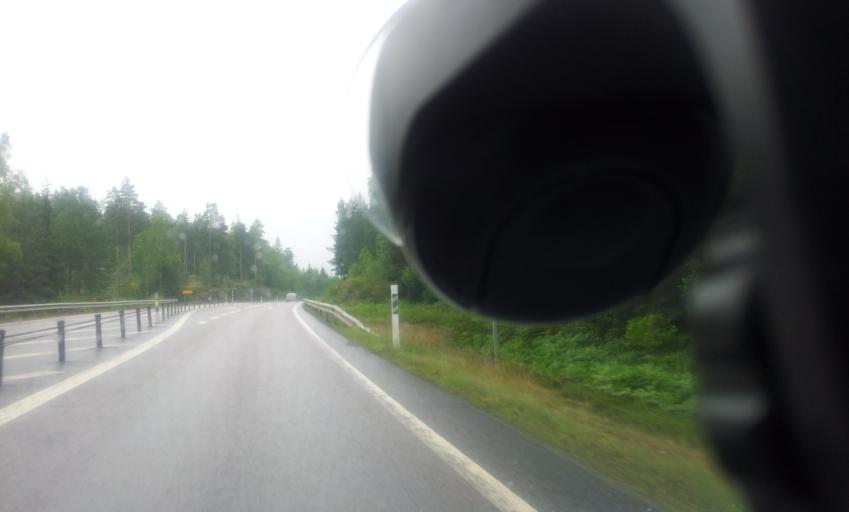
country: SE
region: Kalmar
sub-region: Vasterviks Kommun
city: Forserum
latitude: 58.0438
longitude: 16.5234
